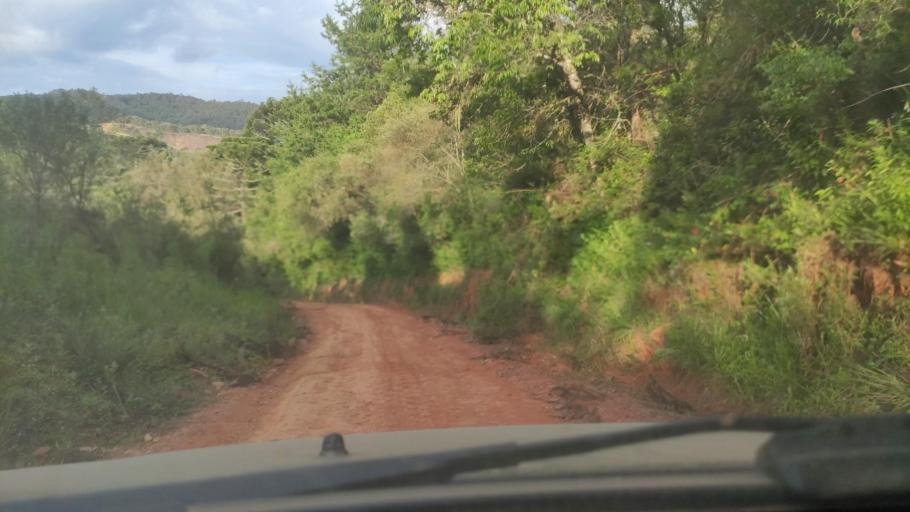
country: BR
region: Minas Gerais
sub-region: Cambui
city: Cambui
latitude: -22.7624
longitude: -45.9603
